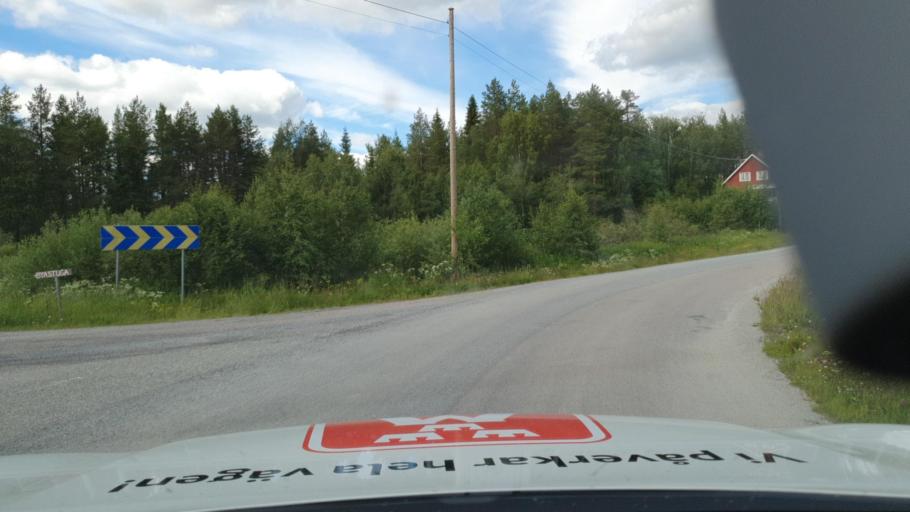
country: SE
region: Vaesterbotten
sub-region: Asele Kommun
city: Insjon
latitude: 64.2010
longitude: 17.7875
